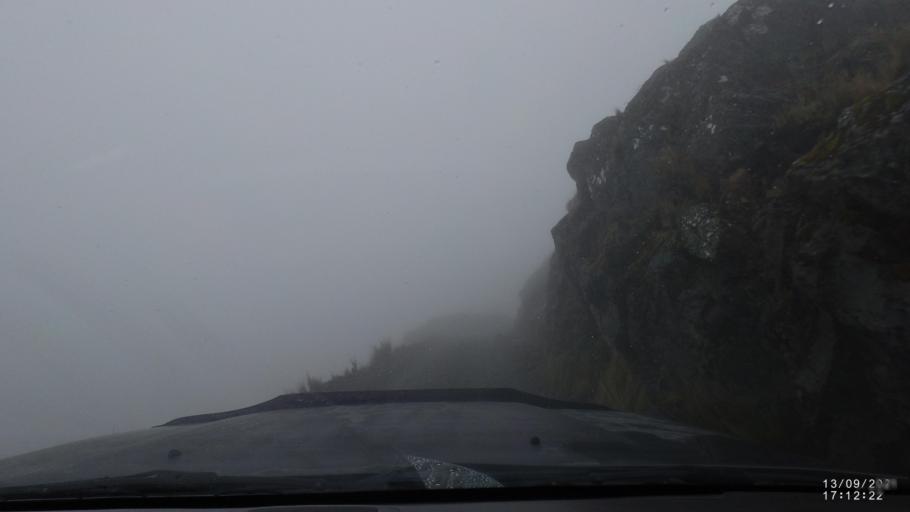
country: BO
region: Cochabamba
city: Colomi
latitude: -17.3385
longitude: -65.7461
